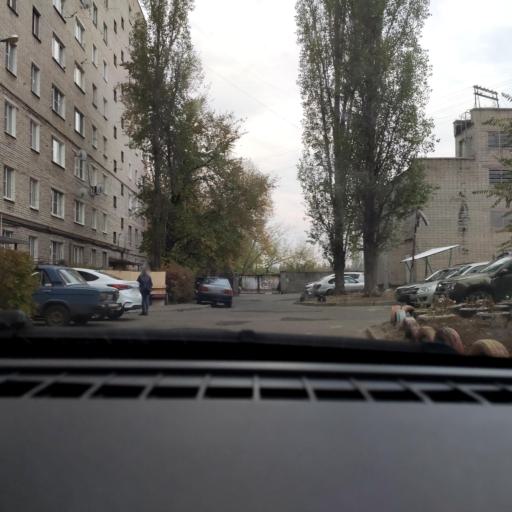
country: RU
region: Voronezj
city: Maslovka
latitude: 51.6149
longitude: 39.2429
